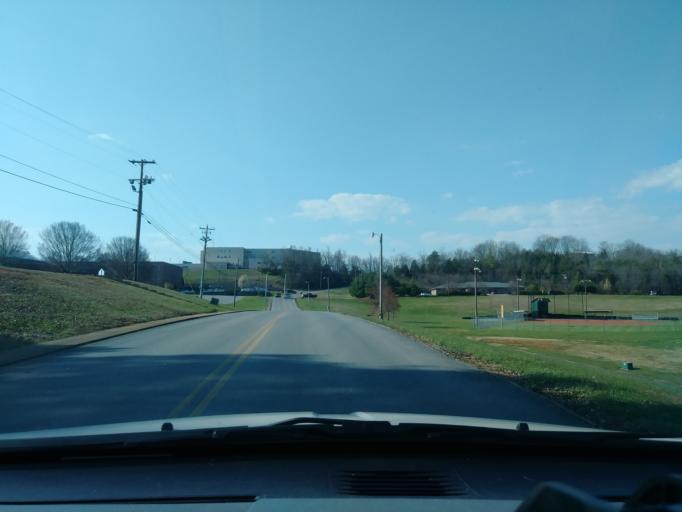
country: US
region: Tennessee
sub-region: Greene County
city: Greeneville
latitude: 36.1489
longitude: -82.8428
